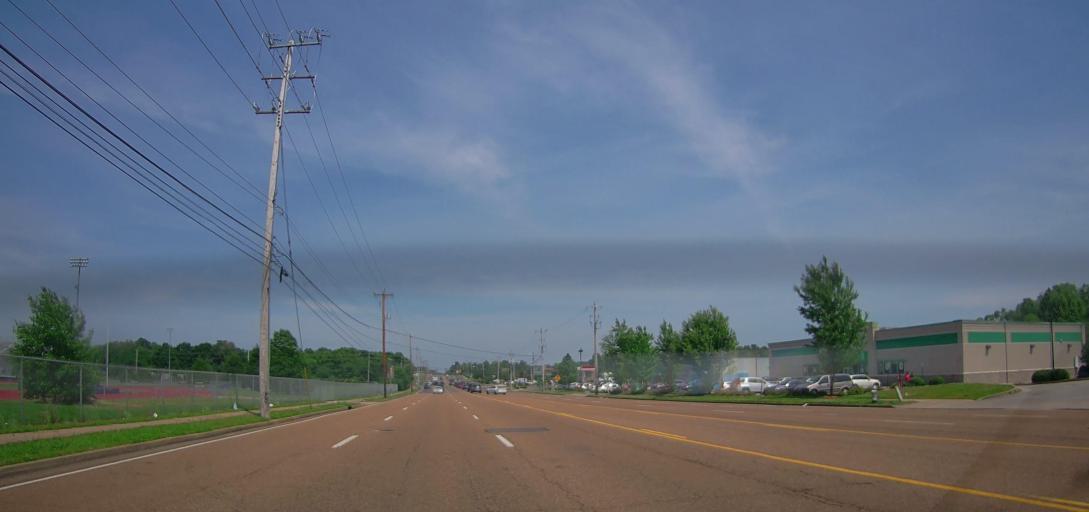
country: US
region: Mississippi
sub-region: De Soto County
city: Olive Branch
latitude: 35.0205
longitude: -89.7989
